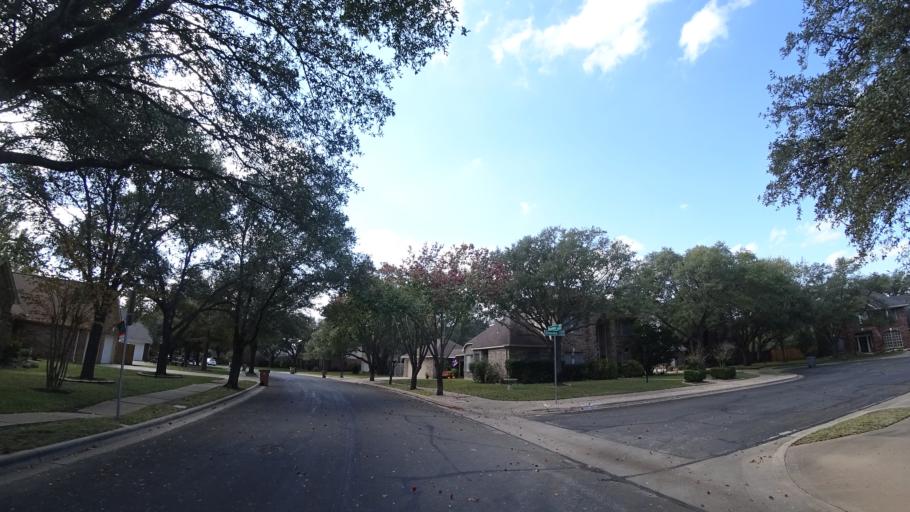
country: US
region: Texas
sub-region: Travis County
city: Shady Hollow
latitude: 30.1835
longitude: -97.8597
